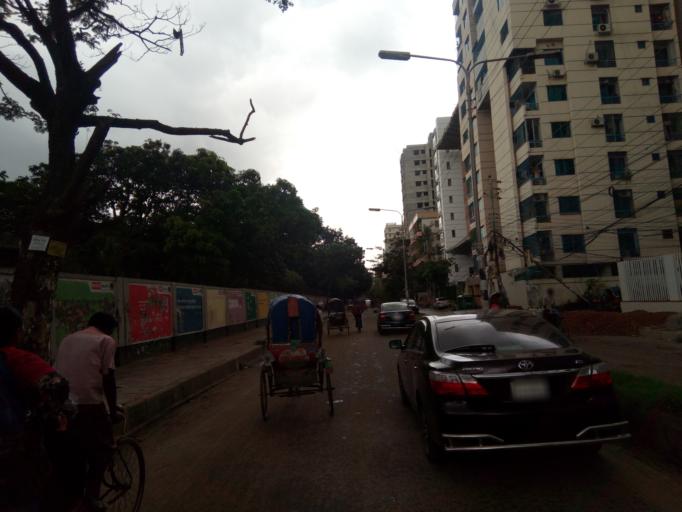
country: BD
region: Dhaka
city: Azimpur
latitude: 23.7661
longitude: 90.3649
